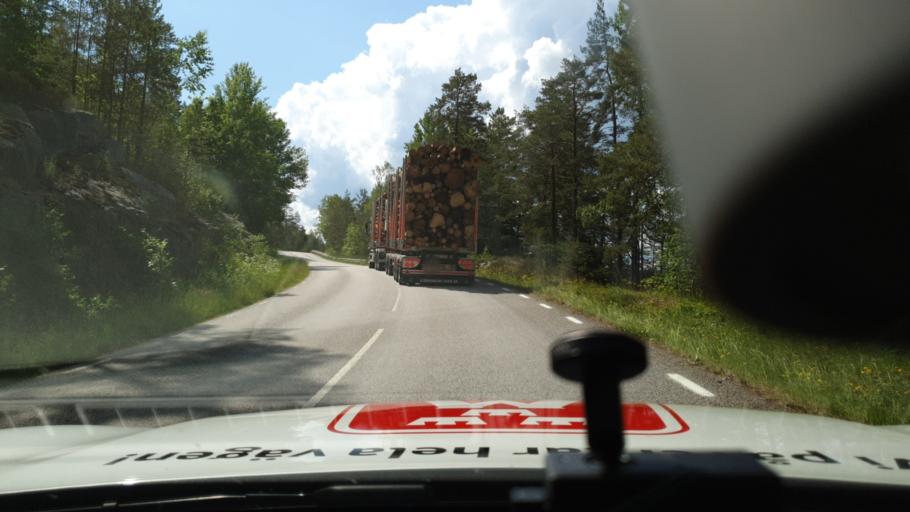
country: SE
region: Kalmar
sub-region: Vasterviks Kommun
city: Gamleby
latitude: 57.8702
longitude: 16.3048
